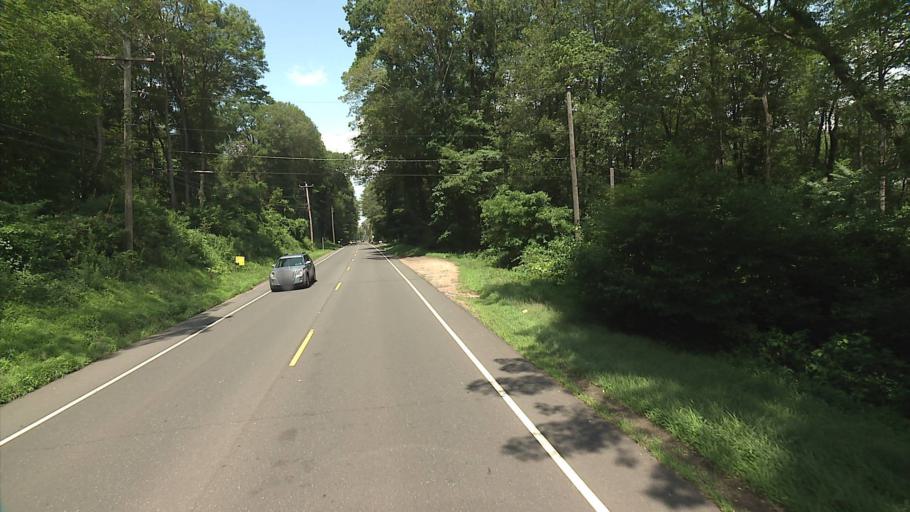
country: US
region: Connecticut
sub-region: Middlesex County
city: East Haddam
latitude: 41.4310
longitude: -72.4535
